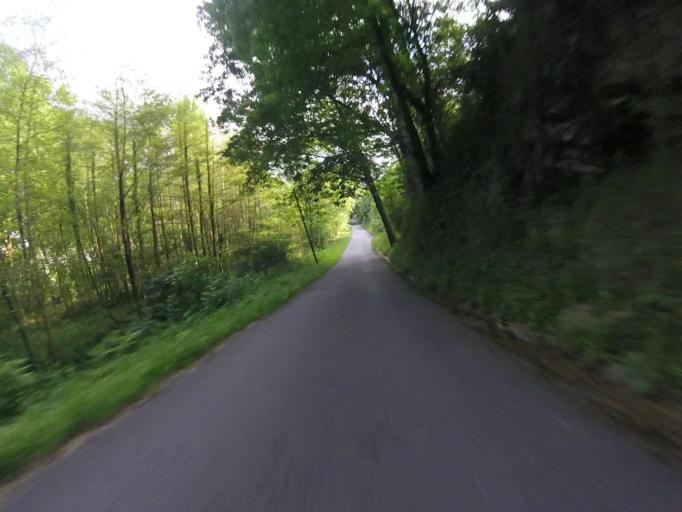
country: ES
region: Basque Country
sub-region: Provincia de Guipuzcoa
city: Astigarraga
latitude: 43.2548
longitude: -1.9500
